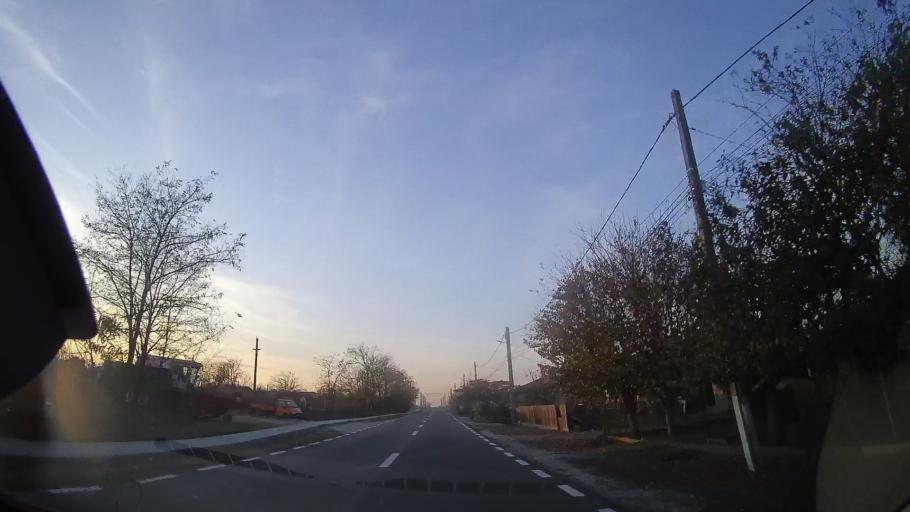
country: RO
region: Constanta
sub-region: Comuna Topraisar
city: Topraisar
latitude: 44.0110
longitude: 28.4442
